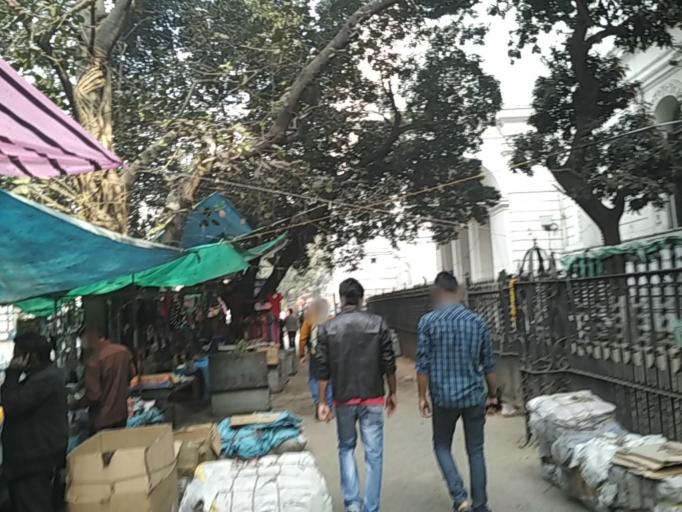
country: IN
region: West Bengal
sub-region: Kolkata
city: Bara Bazar
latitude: 22.5577
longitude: 88.3506
